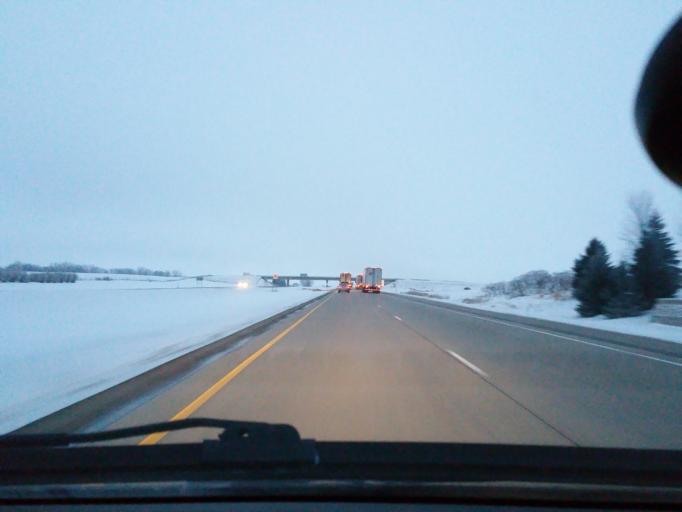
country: US
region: Minnesota
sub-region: Freeborn County
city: Albert Lea
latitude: 43.5042
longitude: -93.3550
